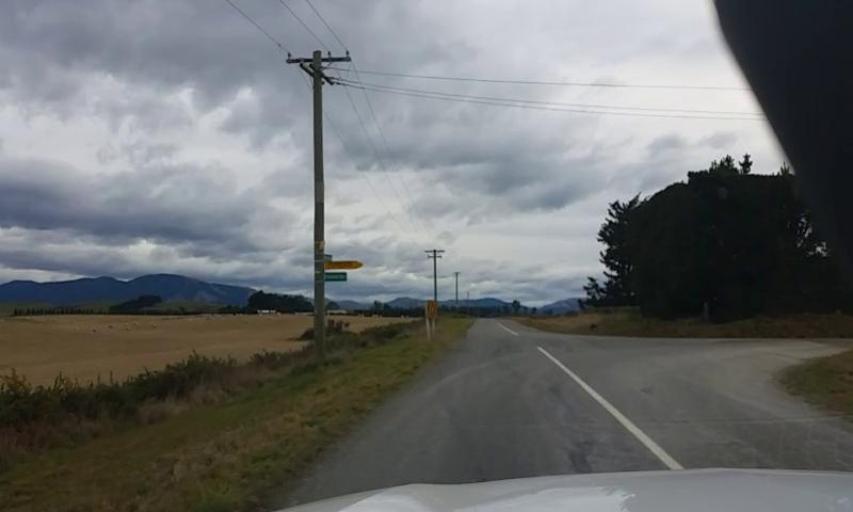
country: NZ
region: Canterbury
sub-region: Waimakariri District
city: Kaiapoi
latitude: -43.2913
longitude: 172.4374
